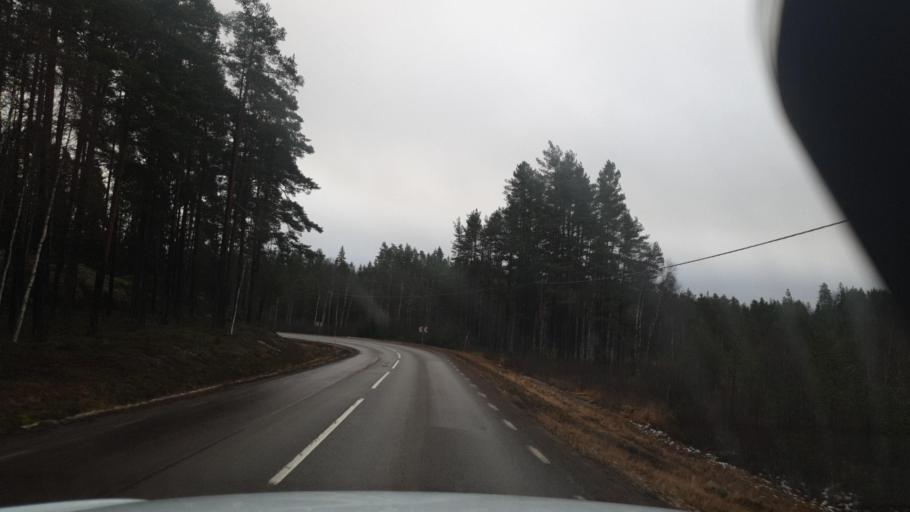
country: SE
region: Vaermland
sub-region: Arjangs Kommun
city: Arjaeng
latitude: 59.5538
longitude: 12.1677
